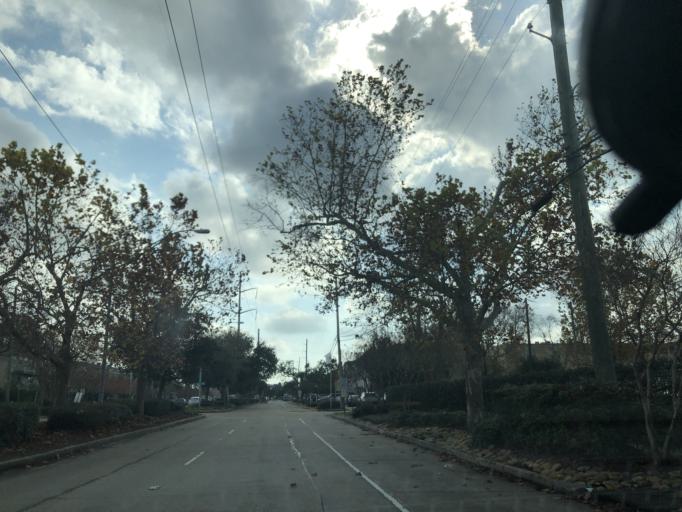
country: US
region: Louisiana
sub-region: Jefferson Parish
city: Metairie
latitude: 29.9948
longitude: -90.1599
